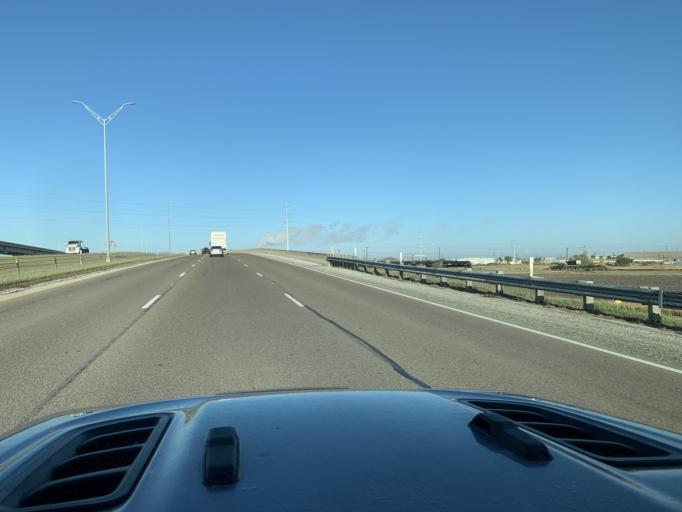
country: US
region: Texas
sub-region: Nueces County
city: Corpus Christi
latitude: 27.7834
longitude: -97.4837
